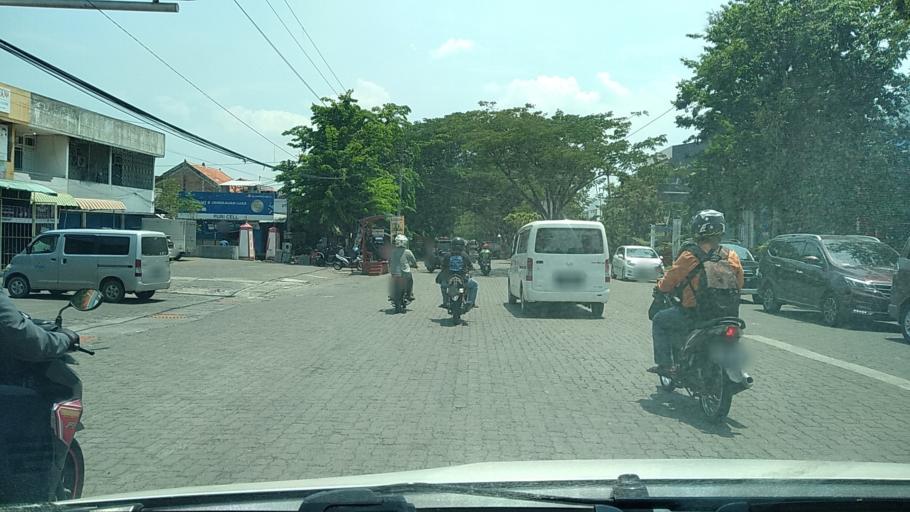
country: ID
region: Central Java
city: Semarang
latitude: -6.9713
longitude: 110.3905
